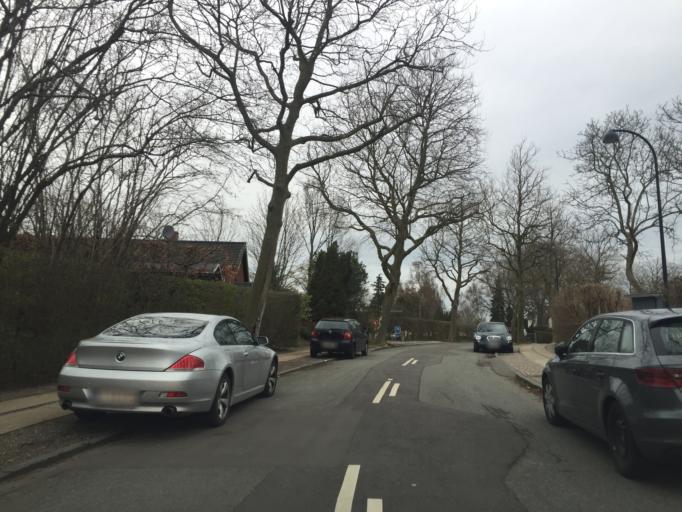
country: DK
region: Capital Region
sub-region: Lyngby-Tarbaek Kommune
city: Kongens Lyngby
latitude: 55.7479
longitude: 12.5434
